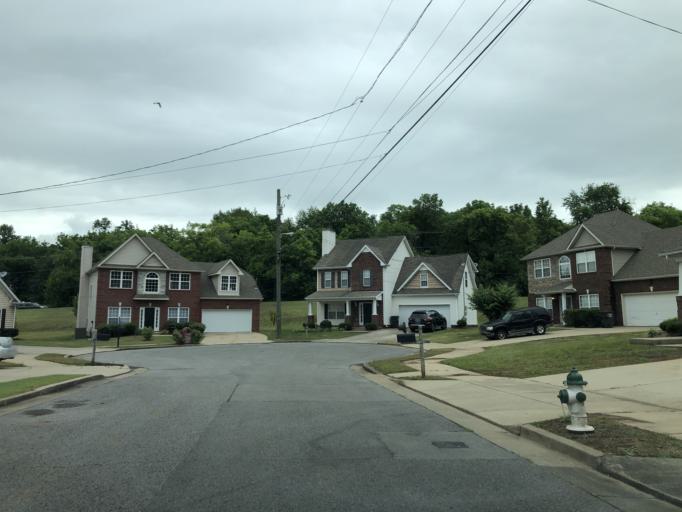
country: US
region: Tennessee
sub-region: Davidson County
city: Goodlettsville
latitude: 36.2756
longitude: -86.7679
